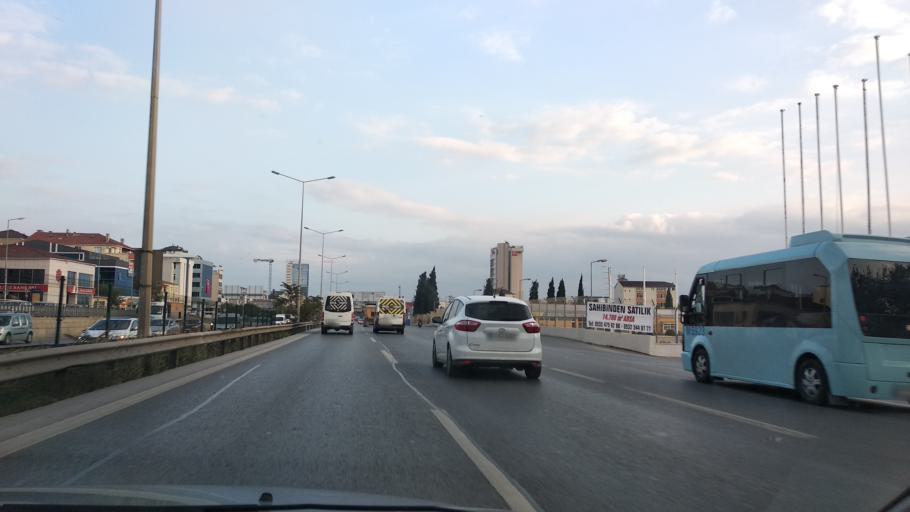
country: TR
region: Istanbul
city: Icmeler
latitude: 40.8528
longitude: 29.2943
